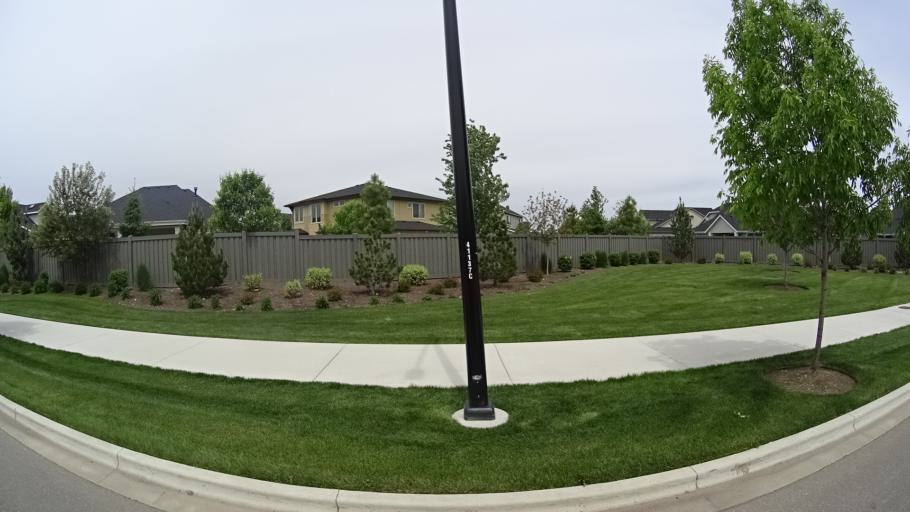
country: US
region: Idaho
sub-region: Ada County
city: Meridian
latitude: 43.5546
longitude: -116.3509
